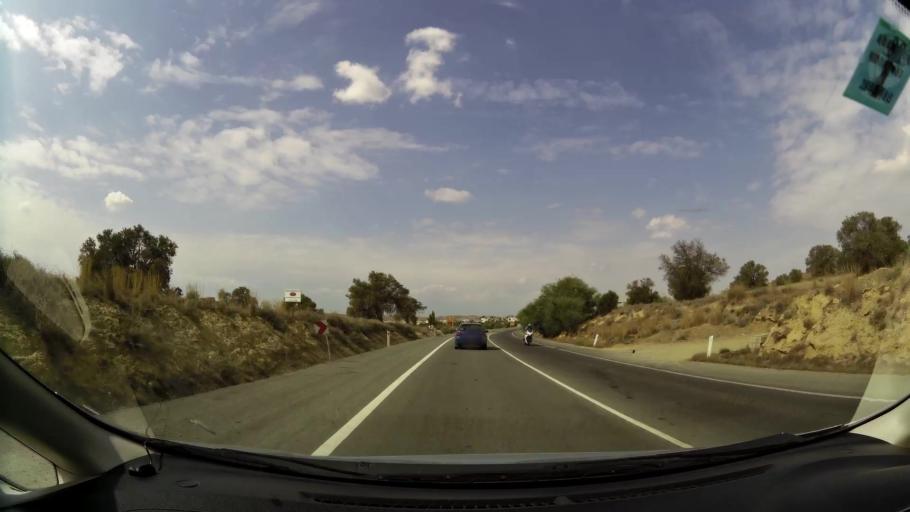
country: CY
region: Lefkosia
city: Tseri
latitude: 35.0649
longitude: 33.3400
